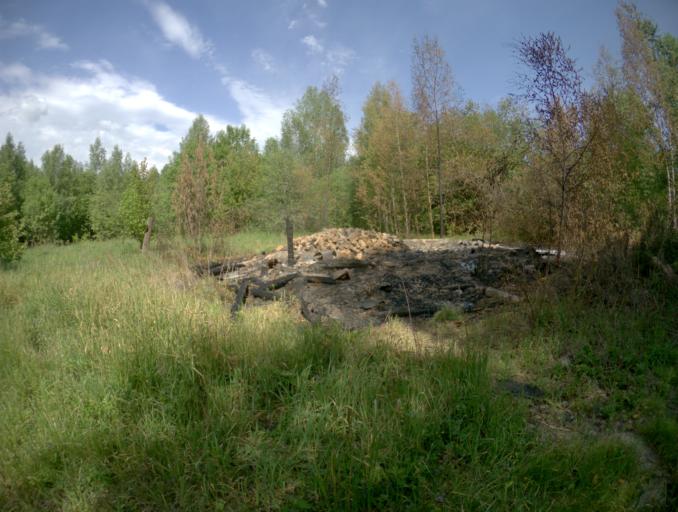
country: RU
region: Vladimir
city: Ivanishchi
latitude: 55.6933
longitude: 40.3758
